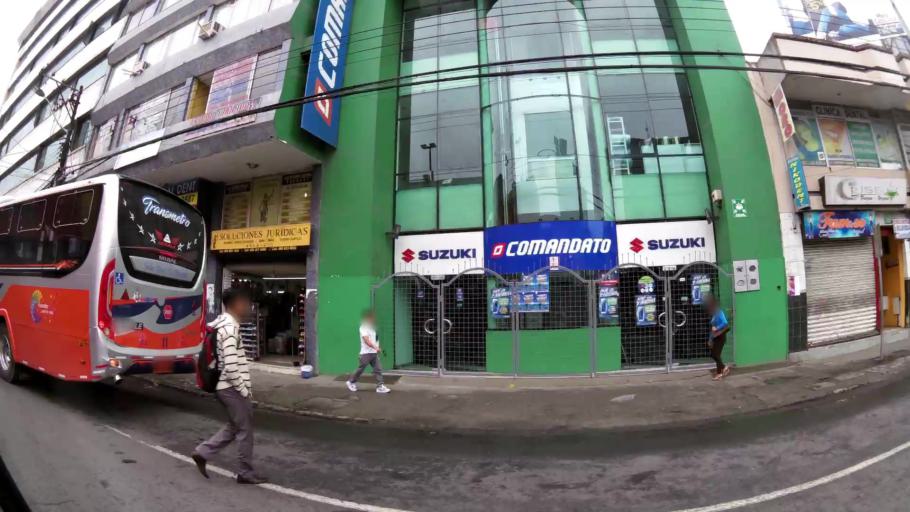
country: EC
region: Santo Domingo de los Tsachilas
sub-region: Canton Santo Domingo de los Colorados
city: Santo Domingo de los Colorados
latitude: -0.2539
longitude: -79.1696
